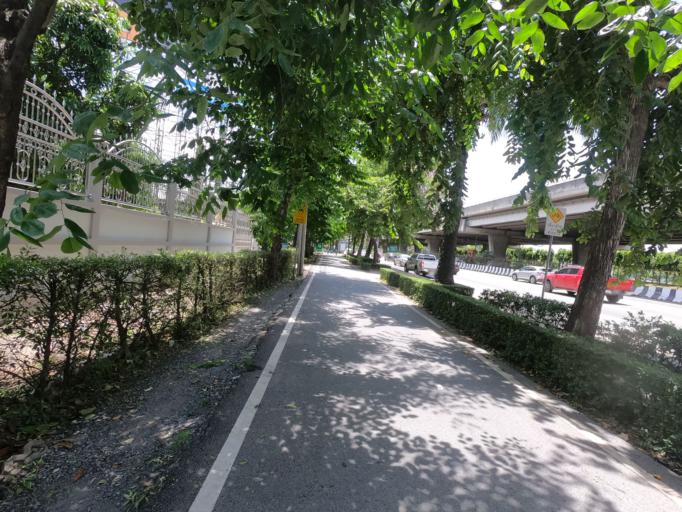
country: TH
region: Bangkok
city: Lat Phrao
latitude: 13.8185
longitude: 100.6241
